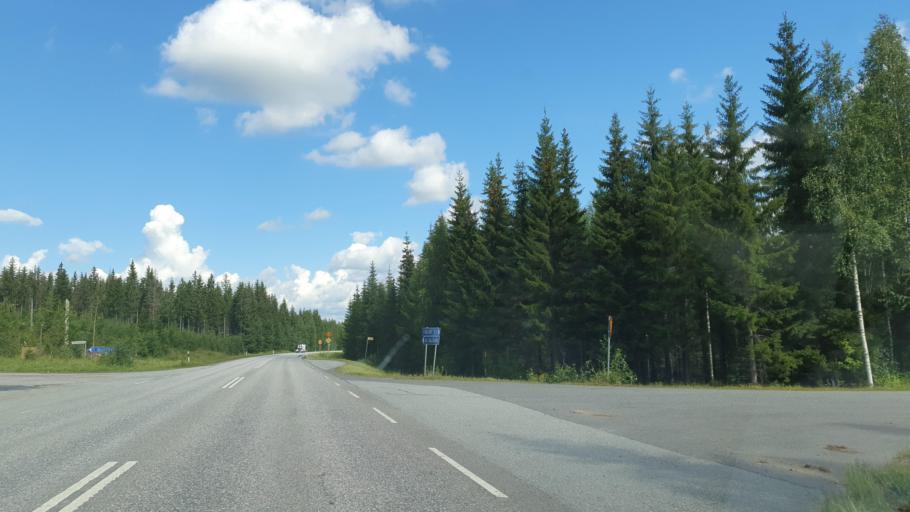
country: FI
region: Northern Savo
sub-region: Ylae-Savo
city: Sonkajaervi
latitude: 63.7464
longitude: 27.3834
